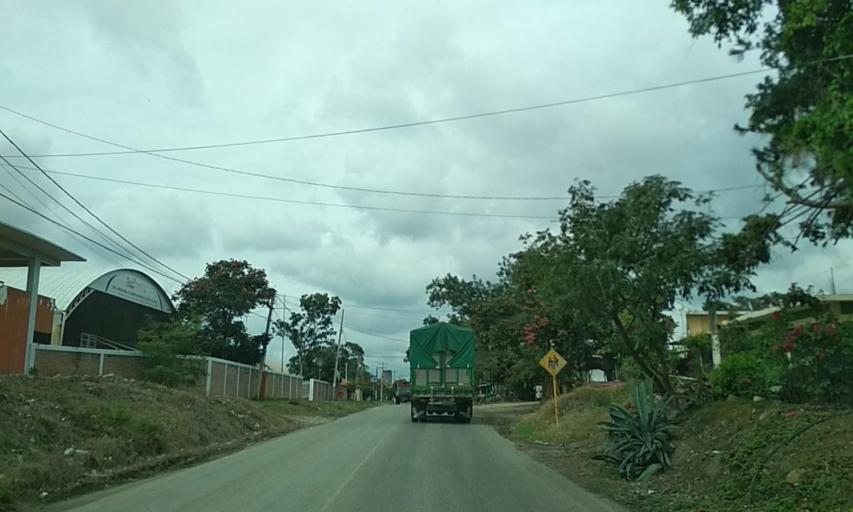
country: MX
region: Veracruz
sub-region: Papantla
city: El Chote
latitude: 20.3715
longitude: -97.3336
